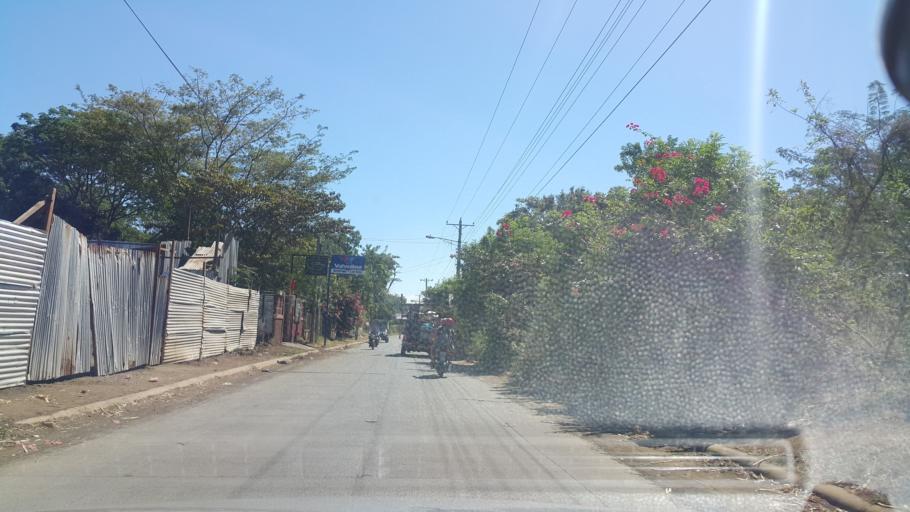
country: NI
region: Masaya
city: Ticuantepe
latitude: 12.0898
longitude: -86.1966
